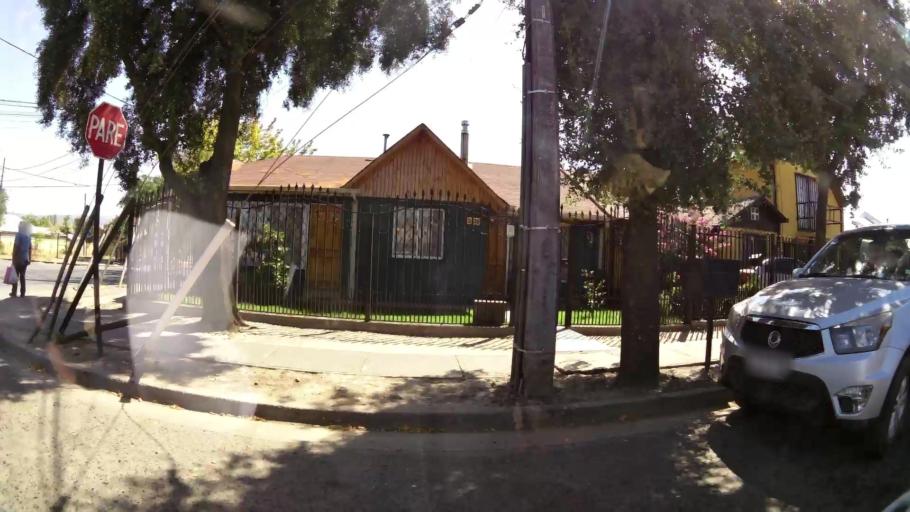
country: CL
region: Maule
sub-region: Provincia de Talca
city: Talca
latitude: -35.4216
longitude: -71.6449
